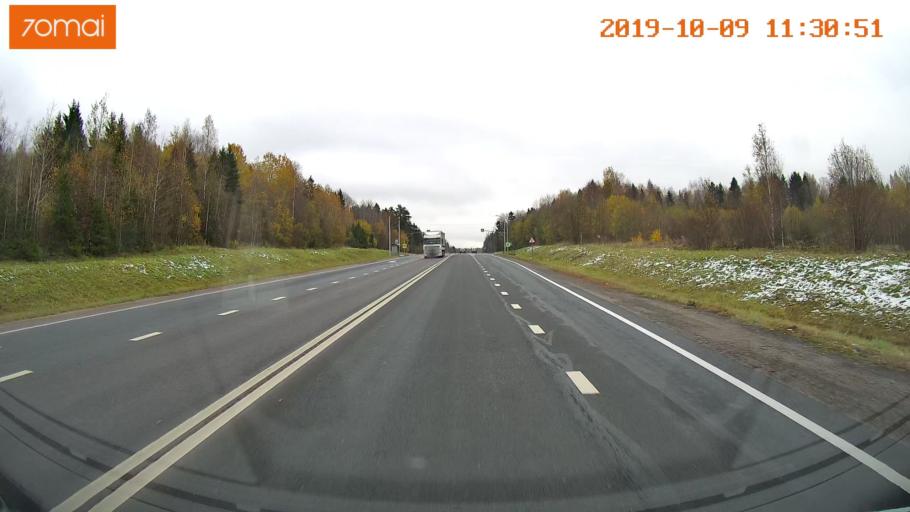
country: RU
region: Vologda
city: Gryazovets
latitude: 59.0504
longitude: 40.0839
